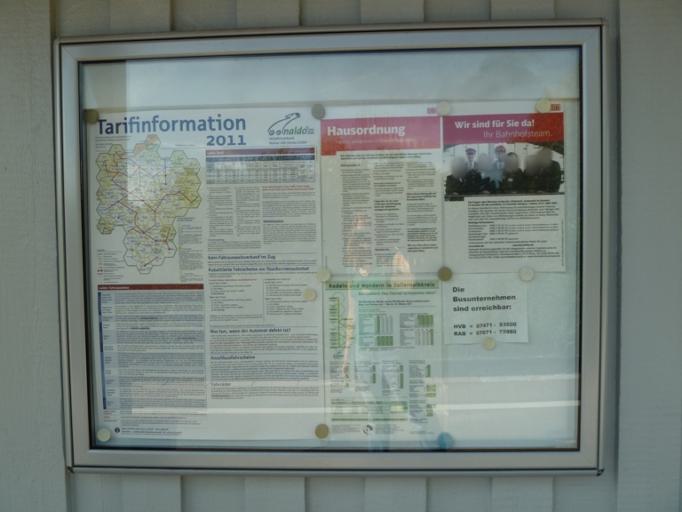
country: DE
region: Baden-Wuerttemberg
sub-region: Tuebingen Region
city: Bodelshausen
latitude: 48.3834
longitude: 8.9906
